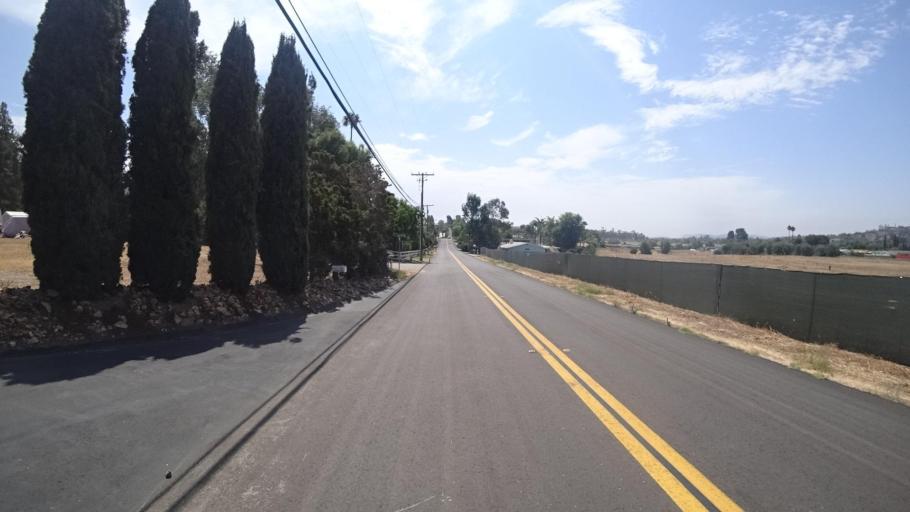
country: US
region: California
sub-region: San Diego County
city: Hidden Meadows
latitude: 33.1775
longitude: -117.0845
